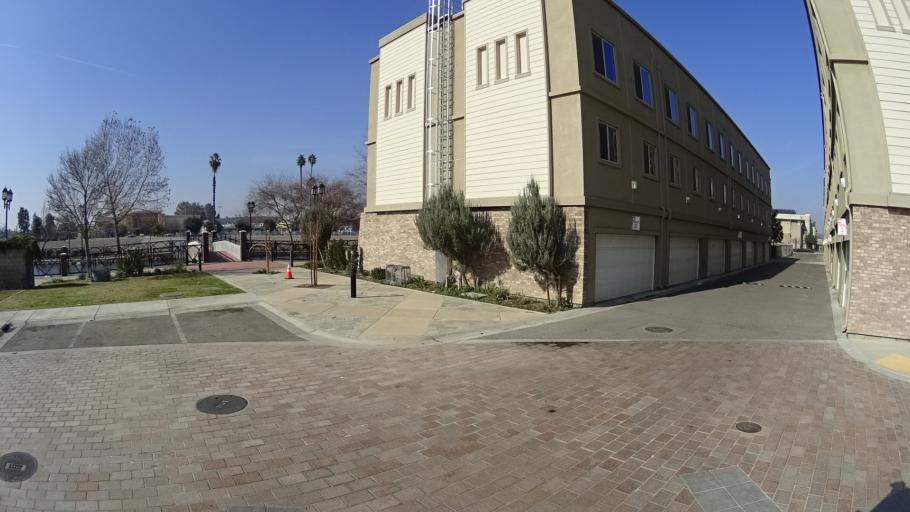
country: US
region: California
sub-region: Kern County
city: Bakersfield
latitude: 35.3694
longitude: -119.0095
